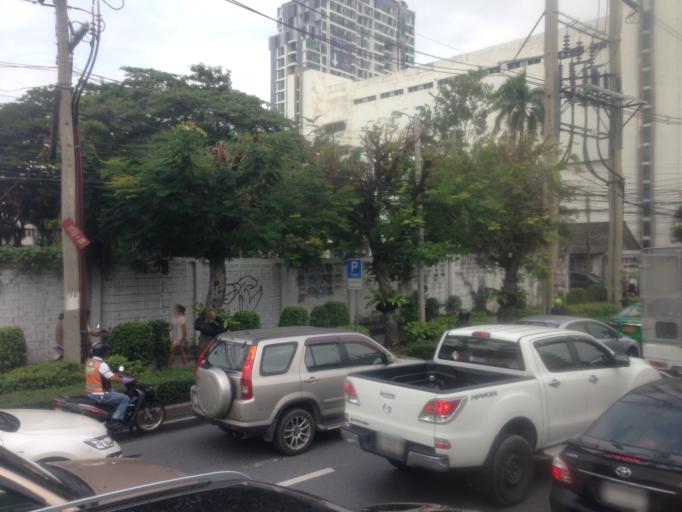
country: TH
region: Bangkok
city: Sathon
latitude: 13.7126
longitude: 100.5347
